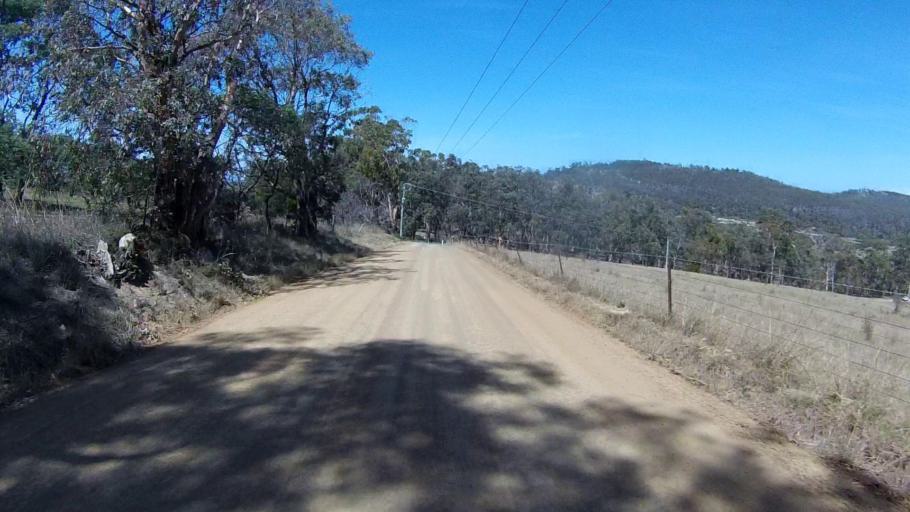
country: AU
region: Tasmania
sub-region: Sorell
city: Sorell
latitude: -42.7825
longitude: 147.6439
